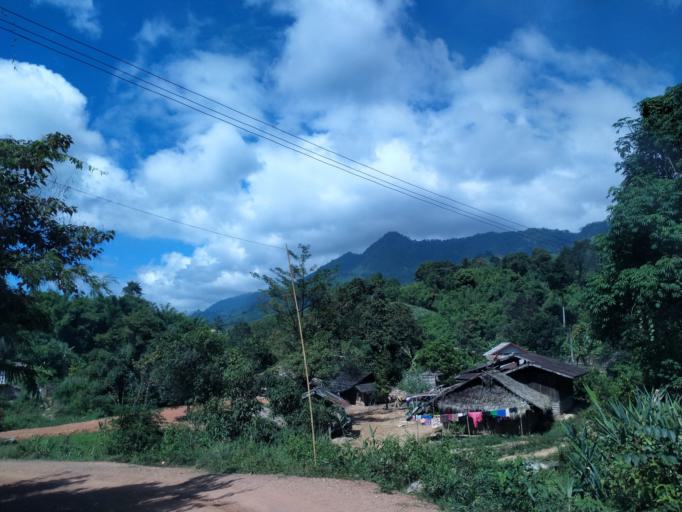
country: TH
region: Nong Khai
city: Rattanawapi
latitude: 18.6373
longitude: 102.9557
